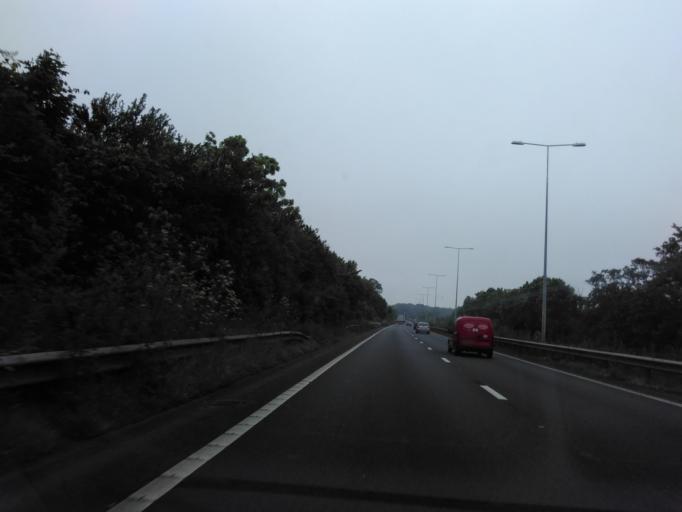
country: GB
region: England
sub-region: Kent
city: Dunkirk
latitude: 51.2948
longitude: 0.9505
